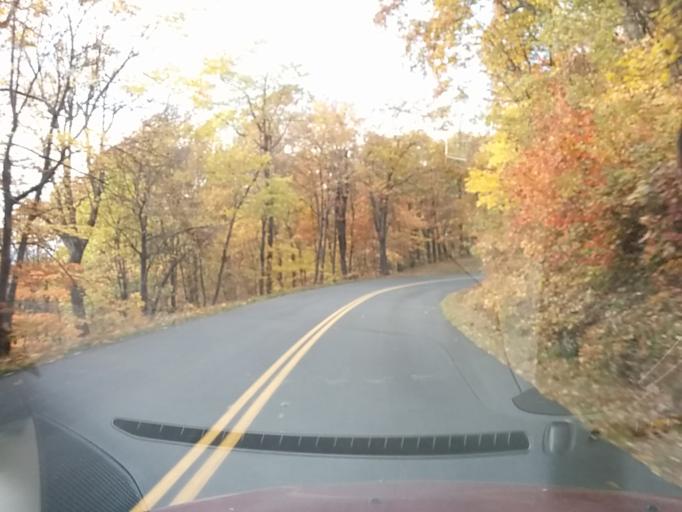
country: US
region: Virginia
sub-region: Augusta County
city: Stuarts Draft
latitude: 37.8867
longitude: -79.0198
